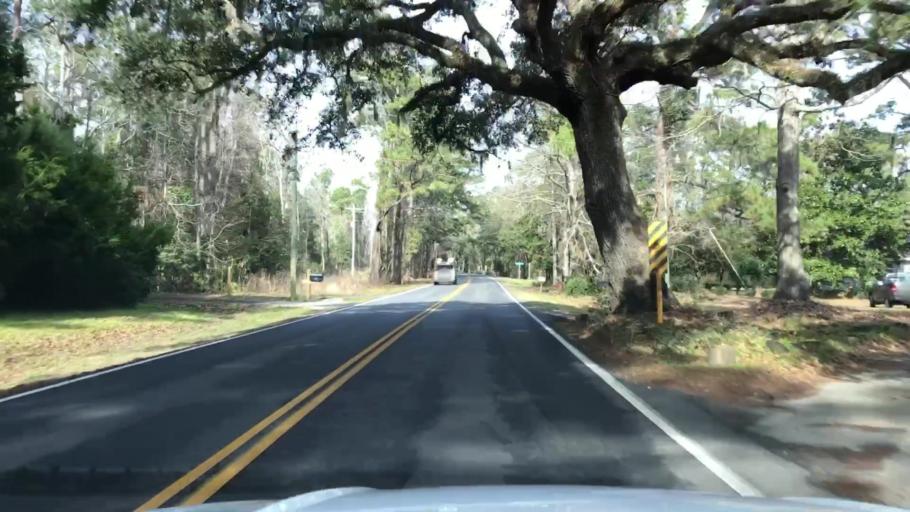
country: US
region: South Carolina
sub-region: Charleston County
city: Folly Beach
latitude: 32.7141
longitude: -80.0191
